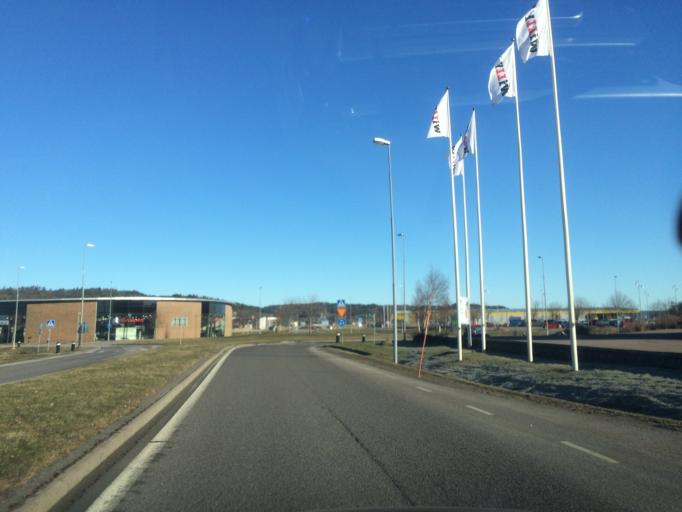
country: SE
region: Halland
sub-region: Kungsbacka Kommun
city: Kungsbacka
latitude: 57.5117
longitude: 12.0810
